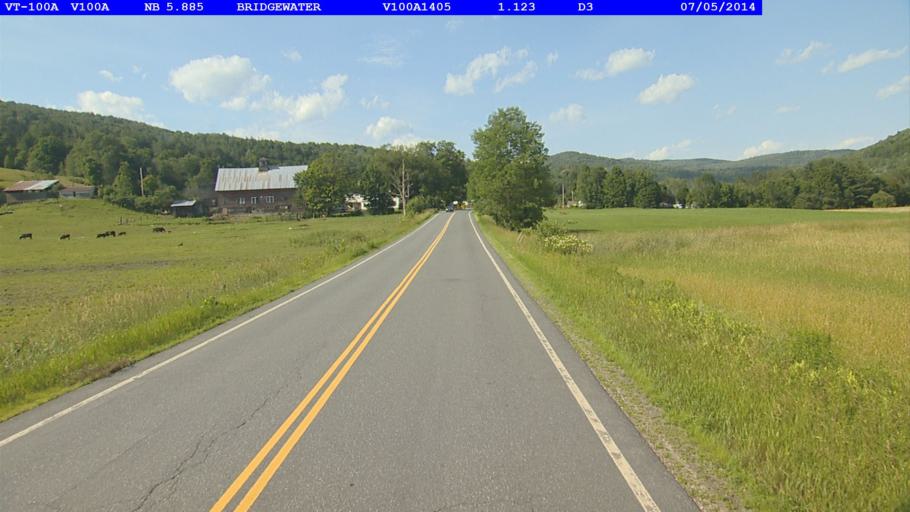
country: US
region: Vermont
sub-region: Windsor County
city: Woodstock
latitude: 43.5742
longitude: -72.6635
